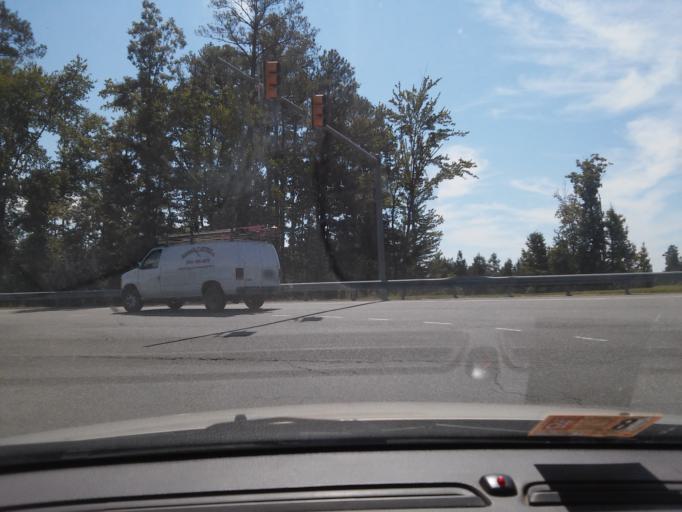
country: US
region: Virginia
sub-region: Henrico County
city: Short Pump
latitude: 37.5594
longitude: -77.6920
